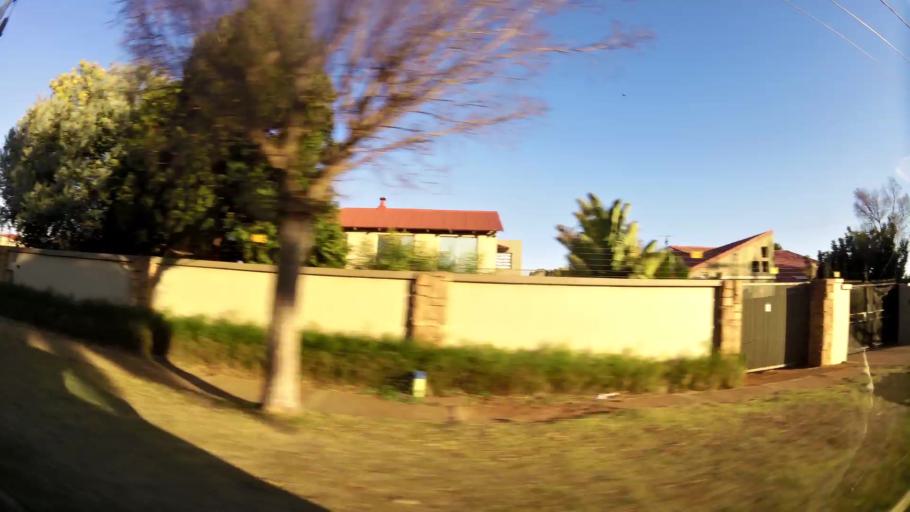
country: ZA
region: Gauteng
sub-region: City of Johannesburg Metropolitan Municipality
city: Roodepoort
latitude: -26.1698
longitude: 27.9274
